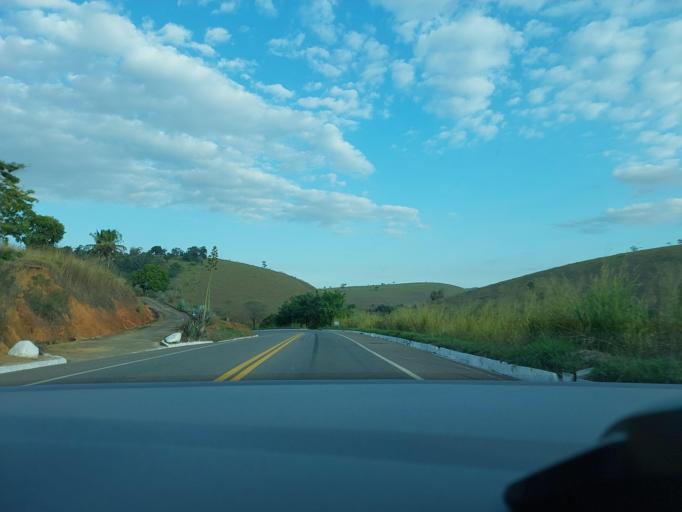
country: BR
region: Minas Gerais
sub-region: Muriae
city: Muriae
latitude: -21.1342
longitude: -42.3163
